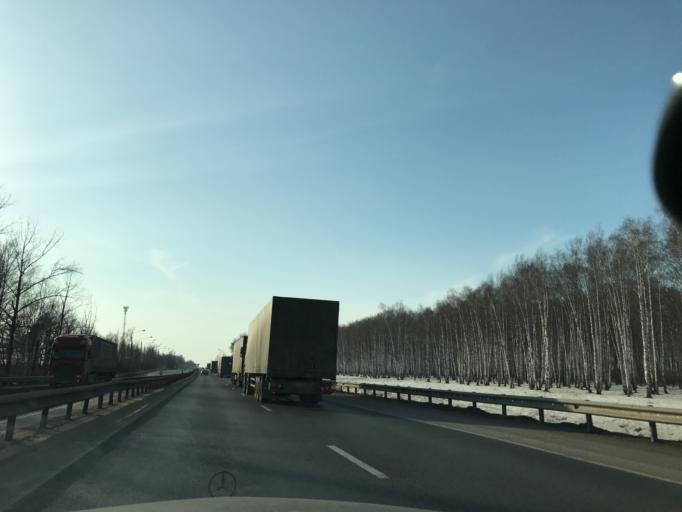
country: RU
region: Vladimir
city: Luknovo
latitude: 56.2389
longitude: 42.0509
